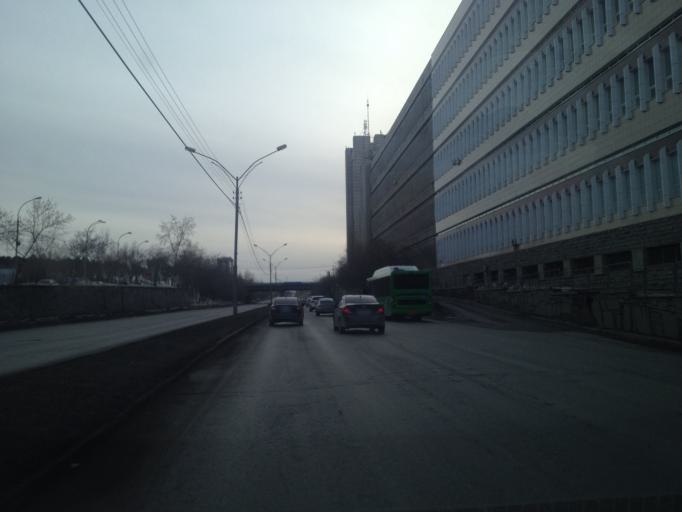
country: RU
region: Sverdlovsk
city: Sovkhoznyy
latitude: 56.8161
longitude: 60.5537
